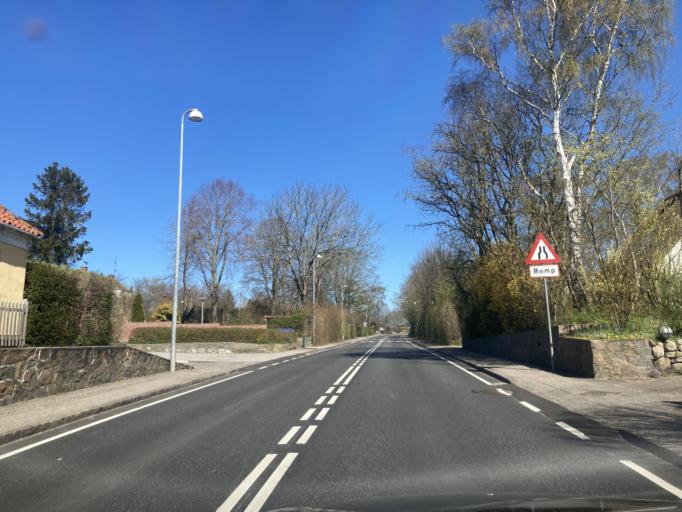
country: DK
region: Capital Region
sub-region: Gribskov Kommune
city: Helsinge
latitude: 56.0868
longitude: 12.2127
